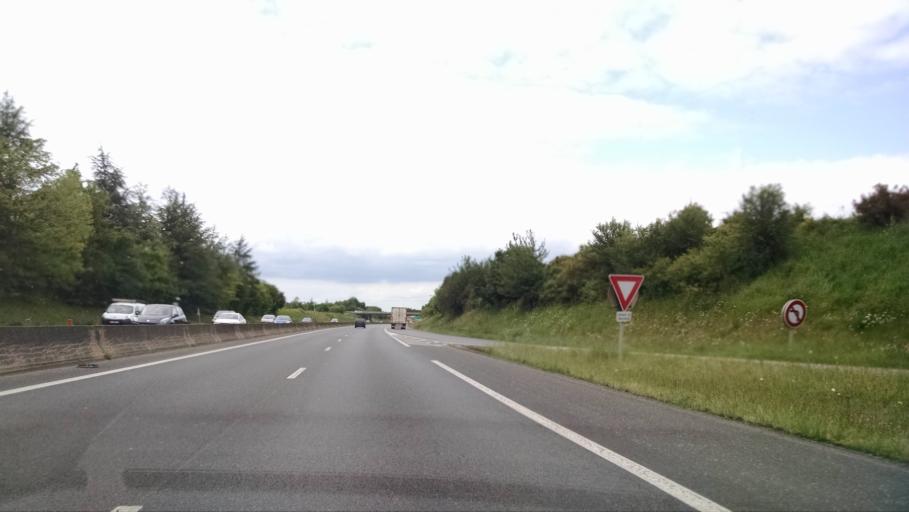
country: FR
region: Pays de la Loire
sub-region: Departement de la Loire-Atlantique
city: Les Sorinieres
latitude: 47.1423
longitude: -1.5137
